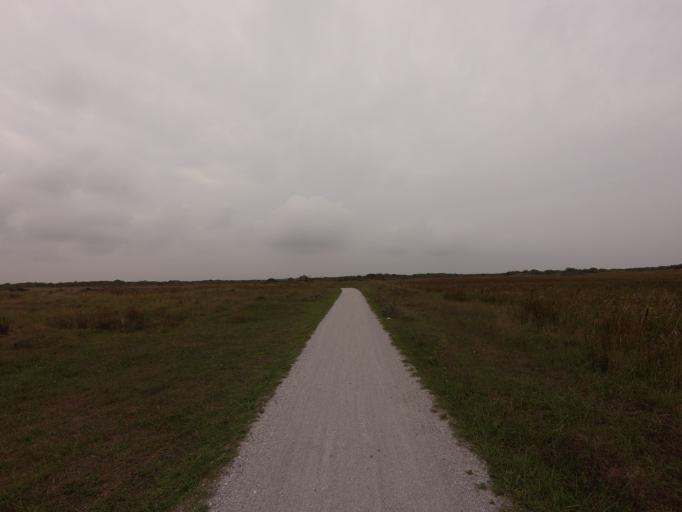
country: NL
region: Friesland
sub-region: Gemeente Schiermonnikoog
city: Schiermonnikoog
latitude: 53.4889
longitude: 6.2065
